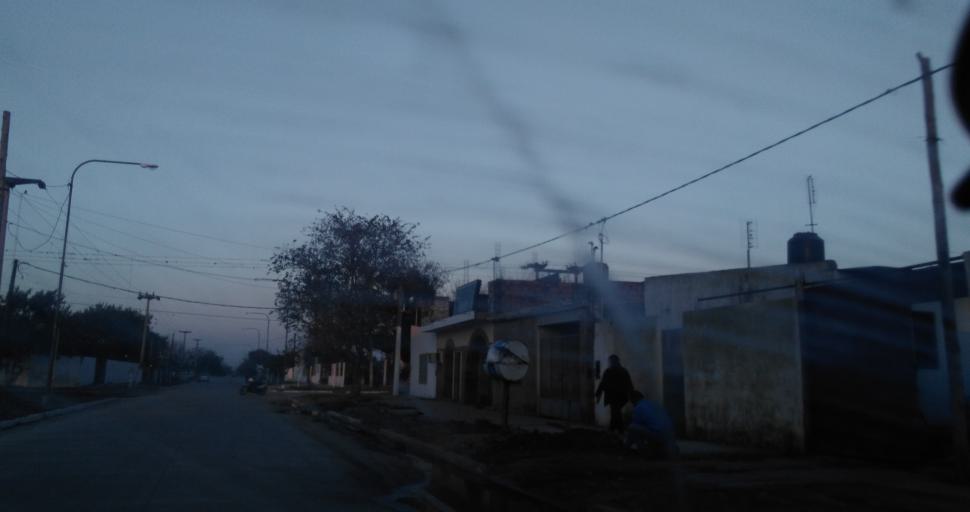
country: AR
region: Chaco
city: Resistencia
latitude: -27.4759
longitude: -58.9647
